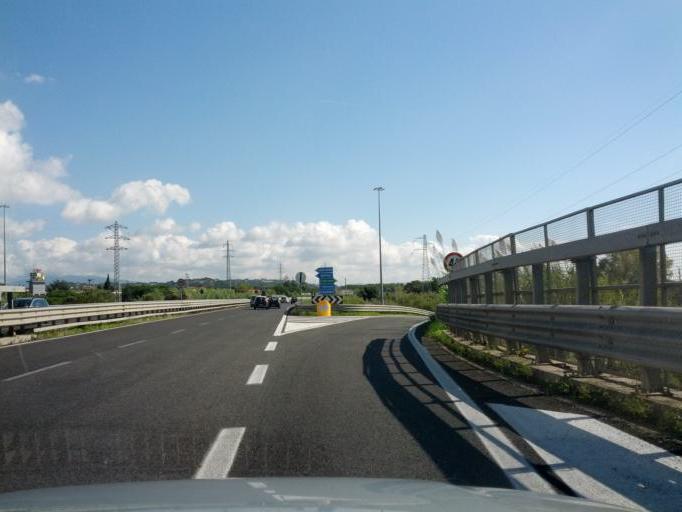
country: IT
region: Latium
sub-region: Provincia di Latina
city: Penitro
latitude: 41.2676
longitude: 13.6813
